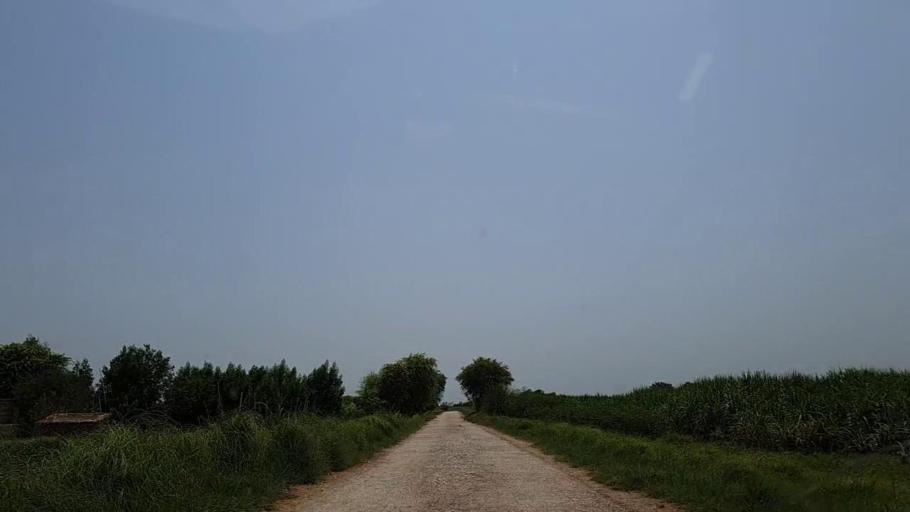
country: PK
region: Sindh
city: Ghotki
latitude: 27.9781
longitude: 69.4021
